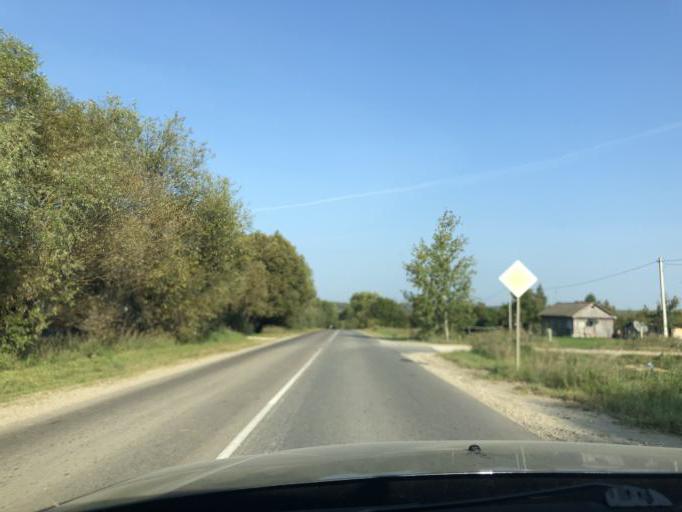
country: RU
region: Tula
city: Leninskiy
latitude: 54.3481
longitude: 37.3579
